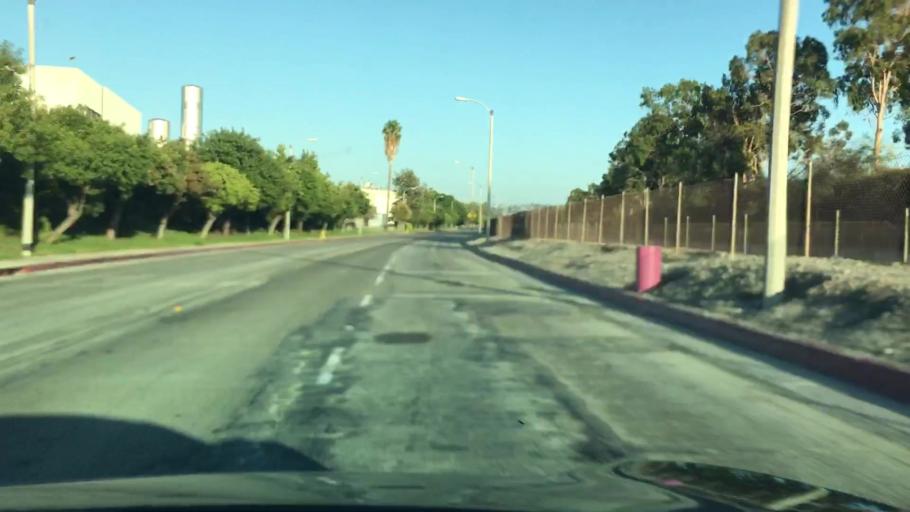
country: US
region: California
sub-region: Los Angeles County
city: South San Jose Hills
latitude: 34.0046
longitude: -117.9076
